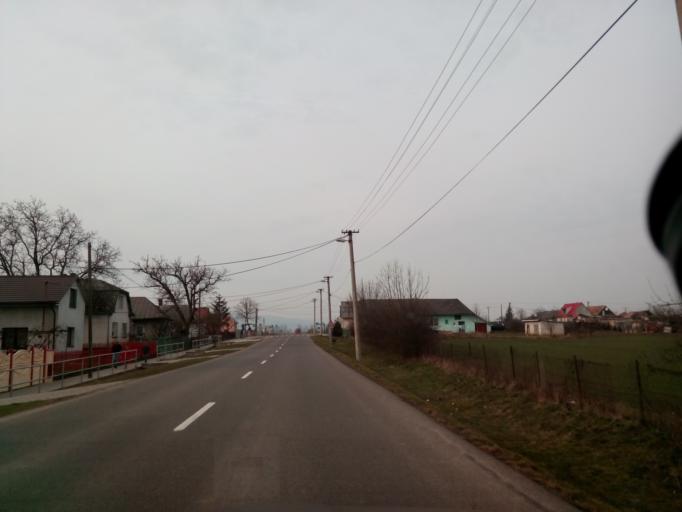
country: SK
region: Kosicky
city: Trebisov
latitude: 48.5873
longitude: 21.6411
